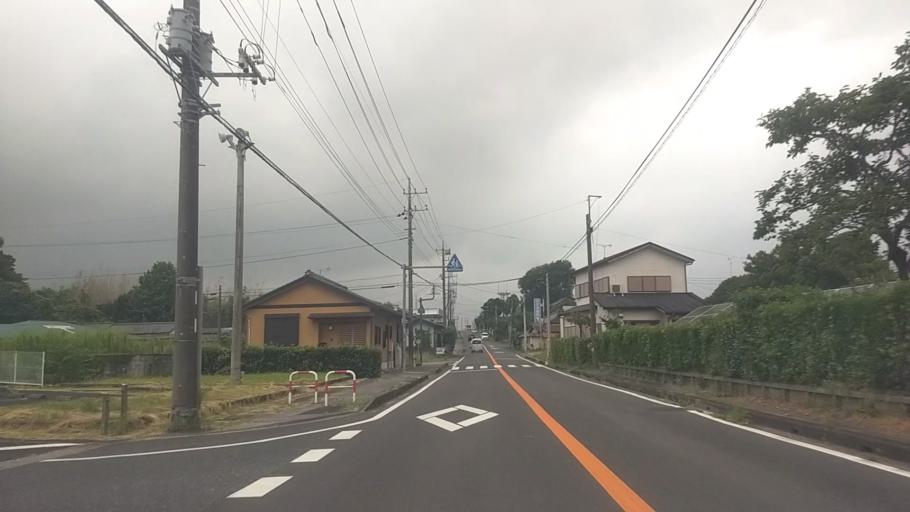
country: JP
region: Chiba
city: Kawaguchi
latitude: 35.1292
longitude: 140.0328
